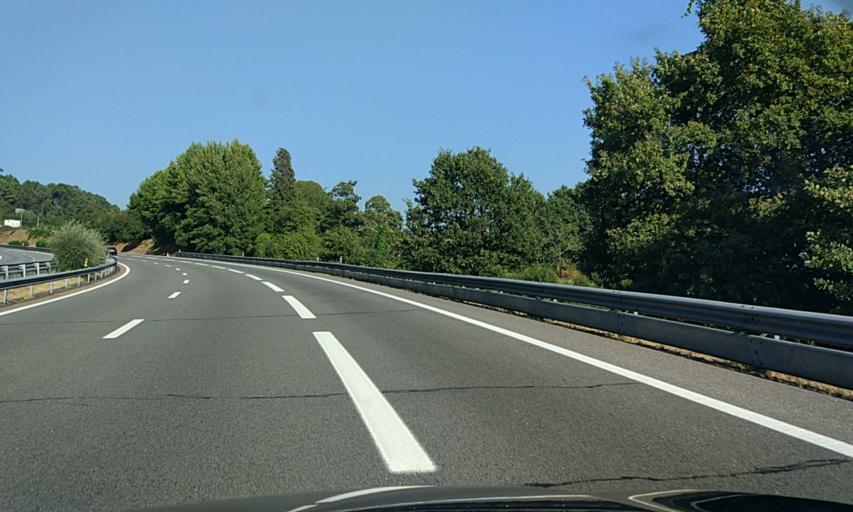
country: PT
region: Porto
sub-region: Marco de Canaveses
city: Marco de Canavezes
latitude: 41.2258
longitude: -8.1548
